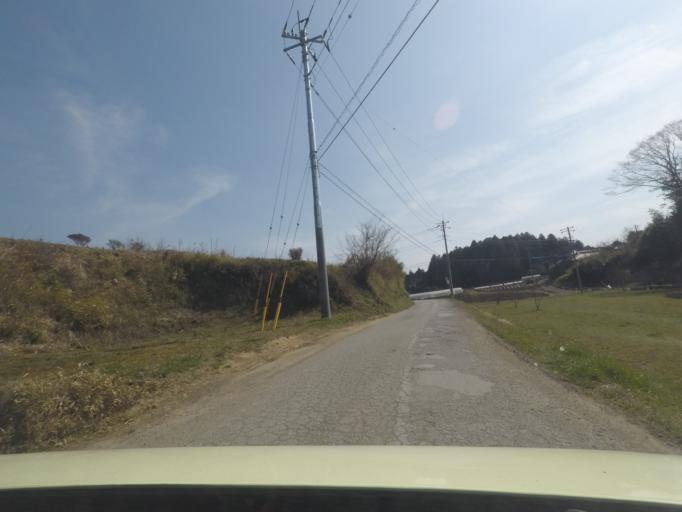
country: JP
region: Ibaraki
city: Ishioka
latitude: 36.1960
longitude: 140.3301
